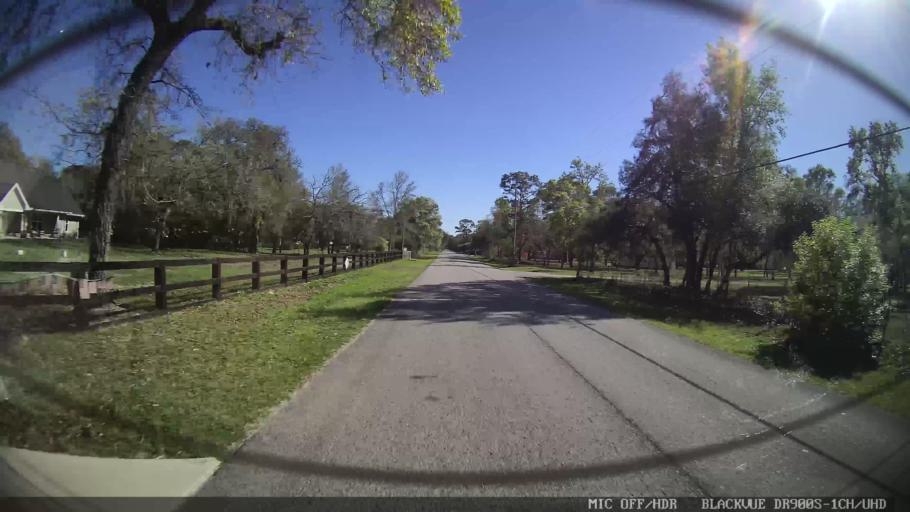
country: US
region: Florida
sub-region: Pasco County
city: Shady Hills
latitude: 28.4102
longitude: -82.5738
